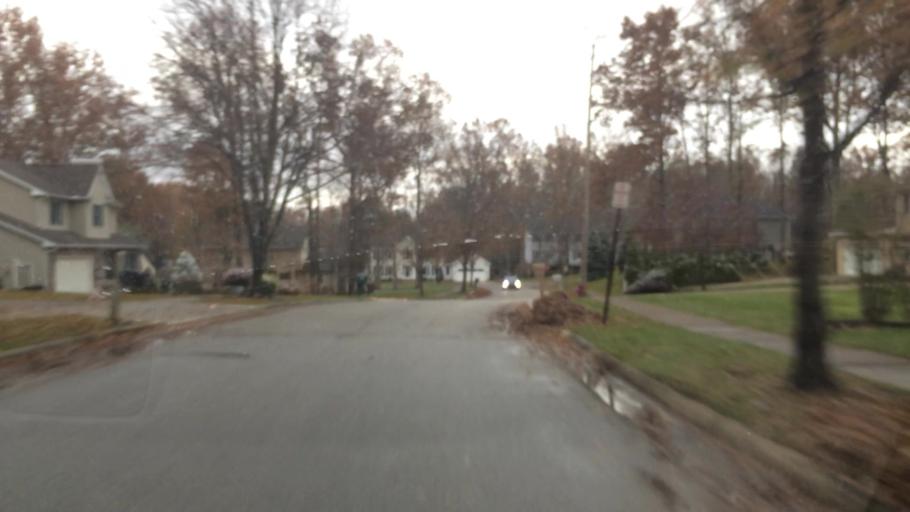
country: US
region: Ohio
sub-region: Summit County
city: Stow
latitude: 41.1773
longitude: -81.4448
